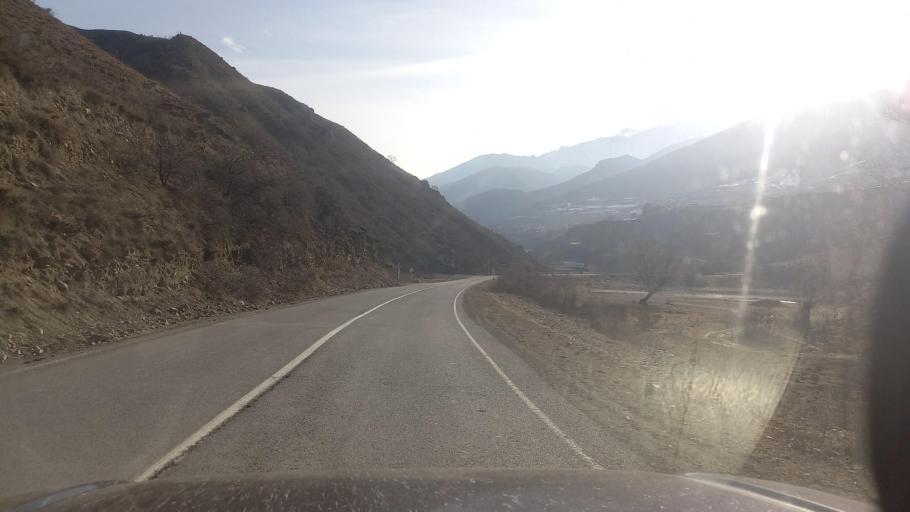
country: RU
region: Ingushetiya
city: Dzhayrakh
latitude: 42.8370
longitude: 44.6611
